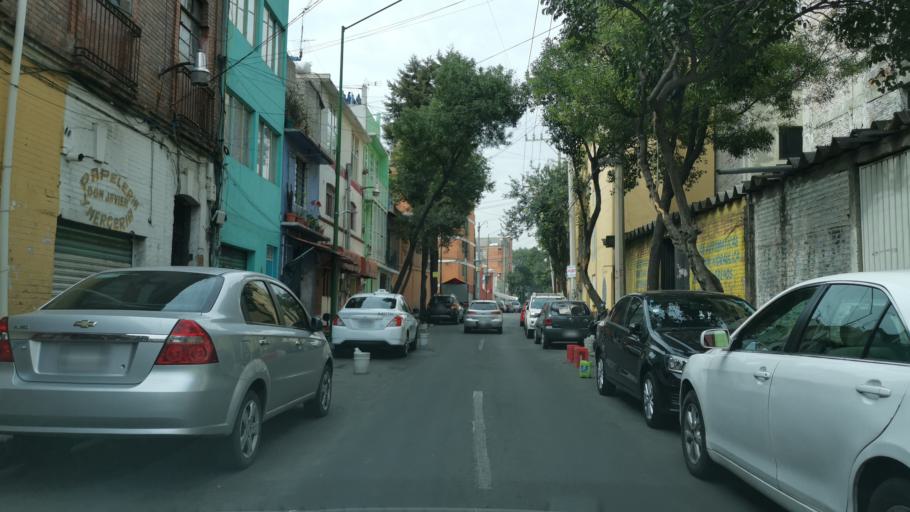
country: MX
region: Mexico City
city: Mexico City
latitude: 19.4213
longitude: -99.1277
